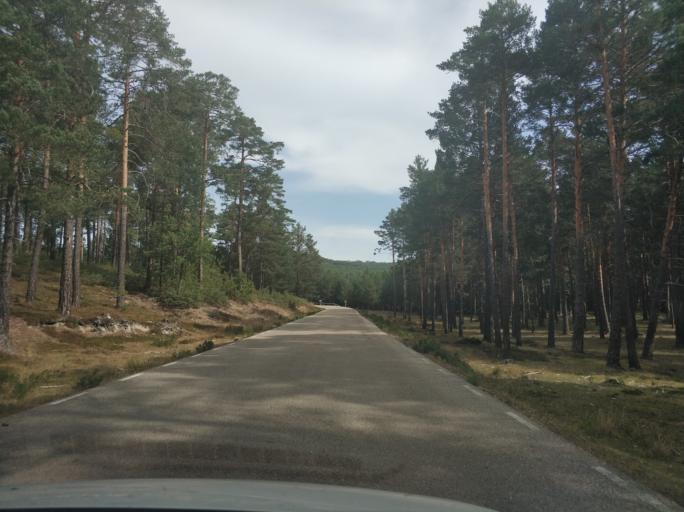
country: ES
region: Castille and Leon
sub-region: Provincia de Soria
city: Navaleno
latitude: 41.8762
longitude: -2.9378
